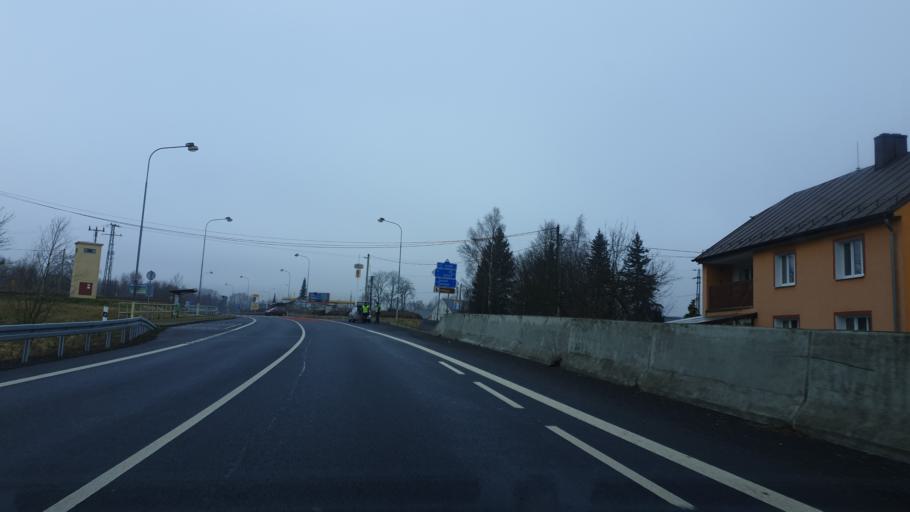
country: CZ
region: Karlovarsky
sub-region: Okres Cheb
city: Skalna
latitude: 50.1650
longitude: 12.3178
